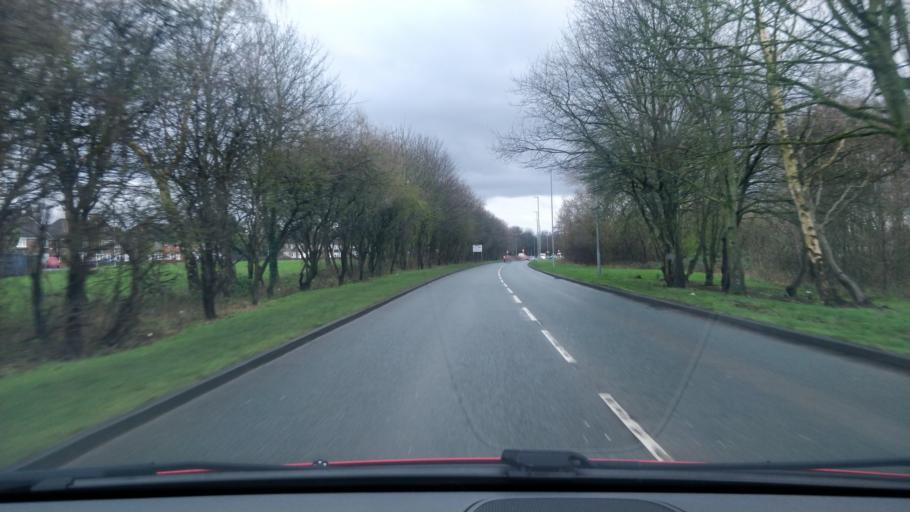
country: GB
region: England
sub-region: Knowsley
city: Huyton
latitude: 53.4268
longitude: -2.8526
